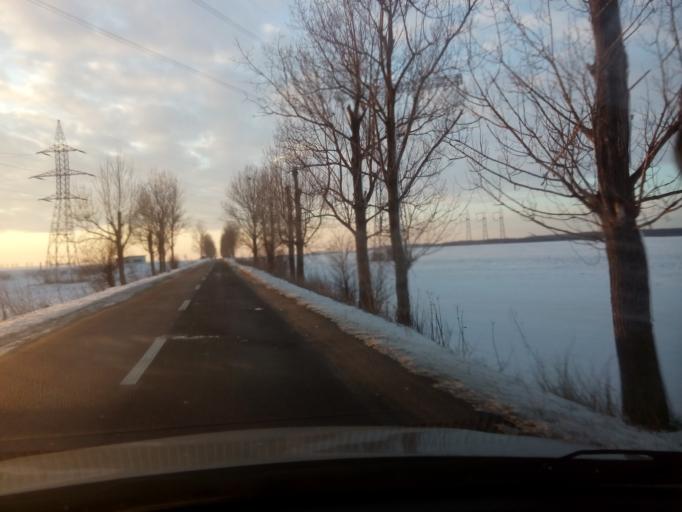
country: RO
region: Calarasi
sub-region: Comuna Luica
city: Luica
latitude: 44.2251
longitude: 26.5664
